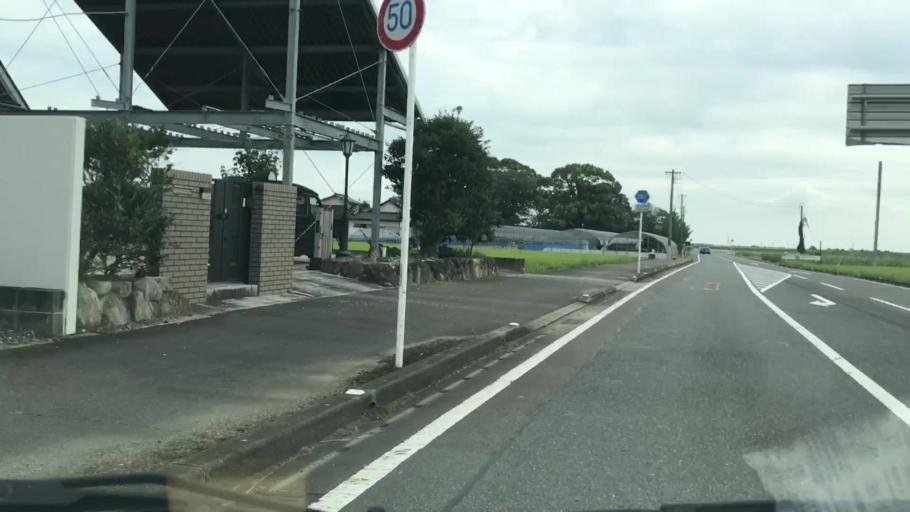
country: JP
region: Saga Prefecture
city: Saga-shi
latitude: 33.2918
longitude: 130.2397
